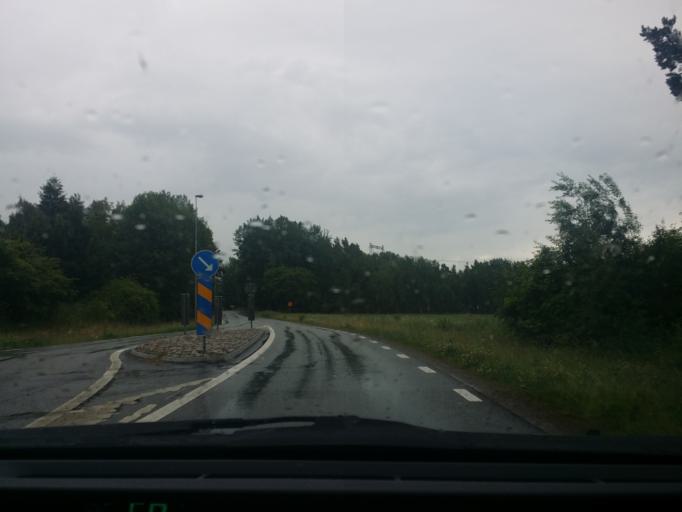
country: SE
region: OErebro
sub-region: Lindesbergs Kommun
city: Fellingsbro
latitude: 59.4283
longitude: 15.5980
